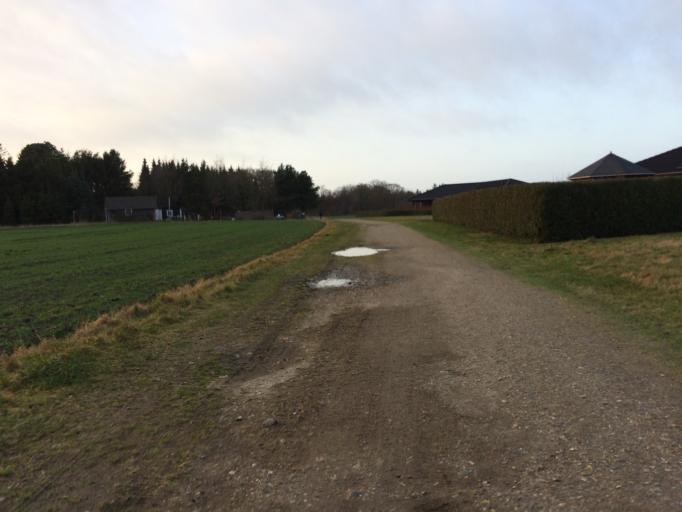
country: DK
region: Central Jutland
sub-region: Holstebro Kommune
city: Ulfborg
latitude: 56.2733
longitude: 8.3055
